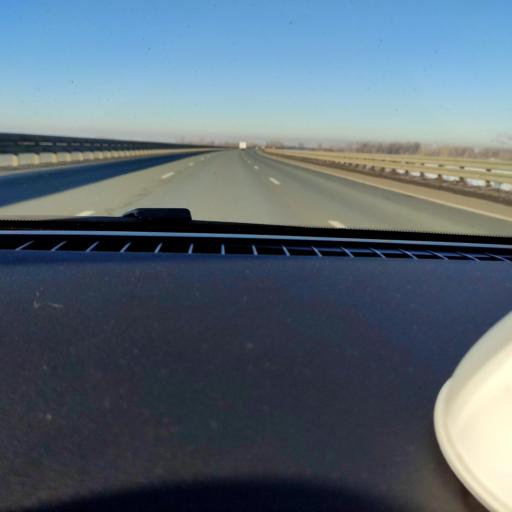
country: RU
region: Samara
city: Smyshlyayevka
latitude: 53.1588
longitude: 50.3328
